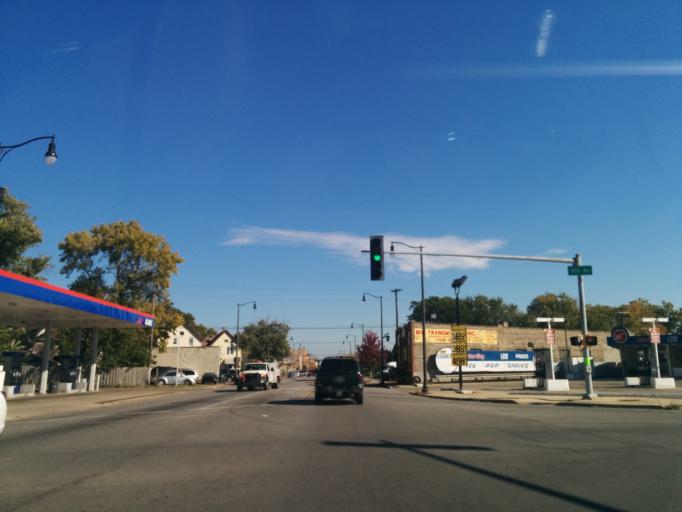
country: US
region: Illinois
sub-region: Cook County
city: Maywood
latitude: 41.8908
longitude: -87.8445
